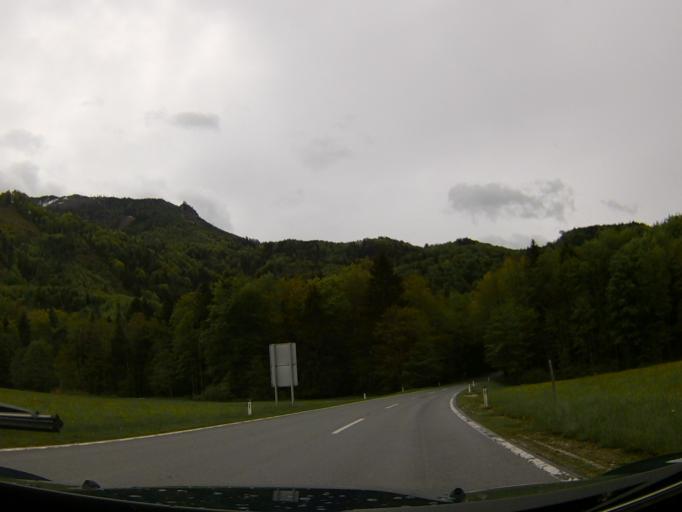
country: AT
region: Upper Austria
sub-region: Politischer Bezirk Vocklabruck
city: Innerschwand
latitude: 47.7961
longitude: 13.3991
